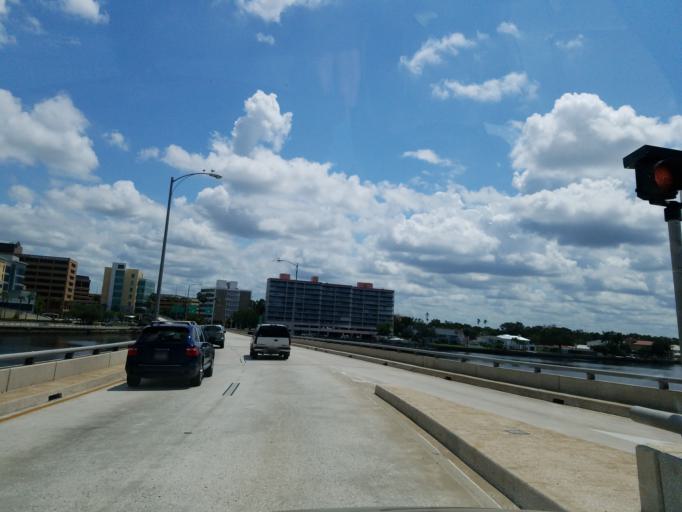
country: US
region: Florida
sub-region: Hillsborough County
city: Tampa
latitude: 27.9374
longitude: -82.4631
